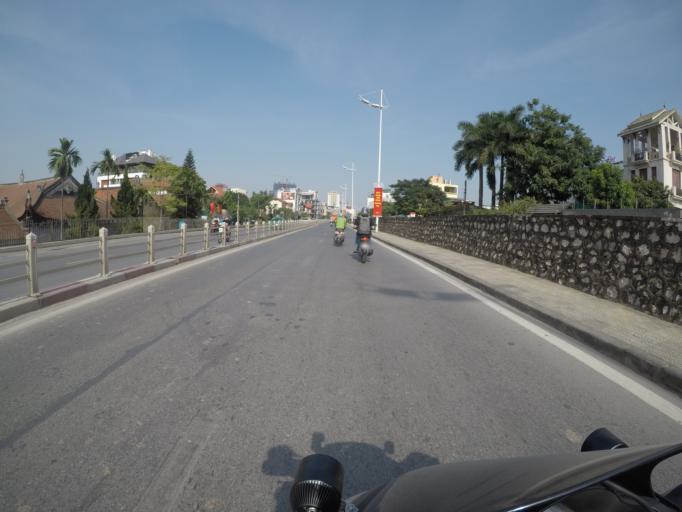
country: VN
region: Ha Noi
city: Tay Ho
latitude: 21.0762
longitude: 105.8218
